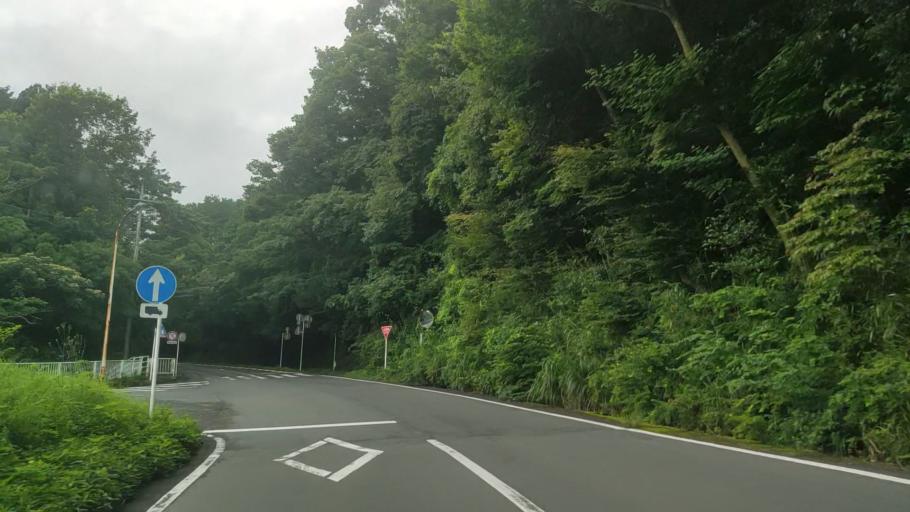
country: JP
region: Shizuoka
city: Fujinomiya
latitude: 35.2030
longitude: 138.5912
